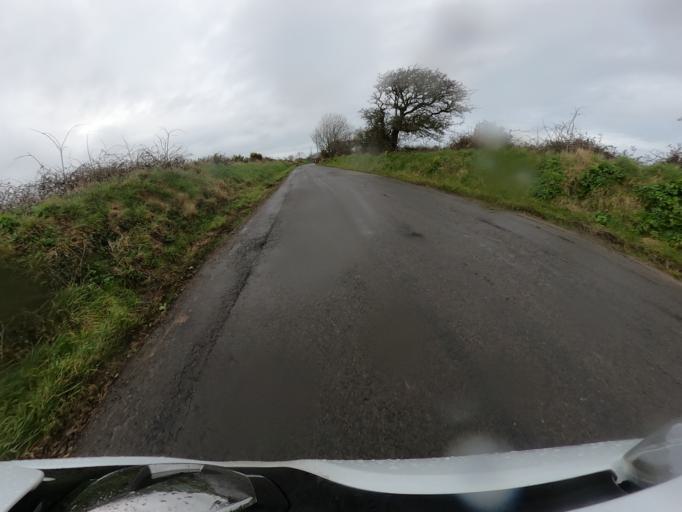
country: IM
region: Ramsey
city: Ramsey
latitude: 54.3733
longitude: -4.4500
